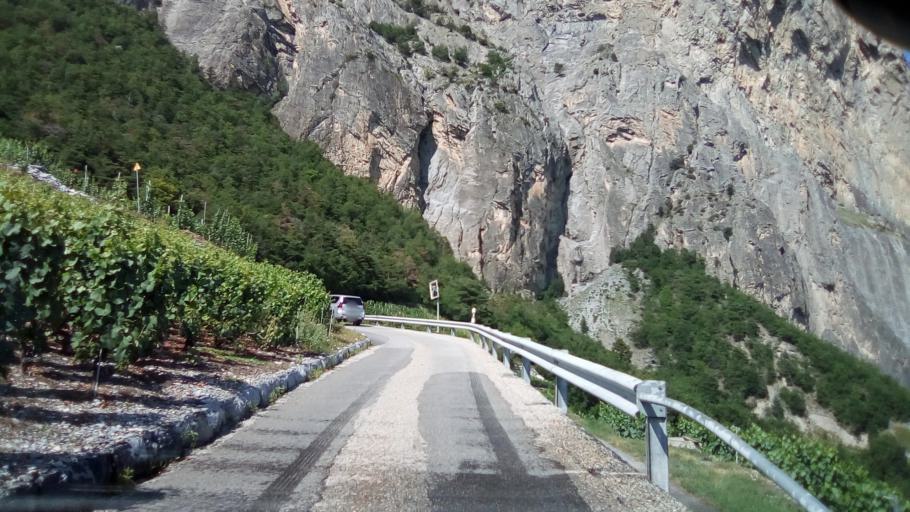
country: CH
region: Valais
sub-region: Conthey District
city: Chamoson
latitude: 46.2076
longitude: 7.2298
